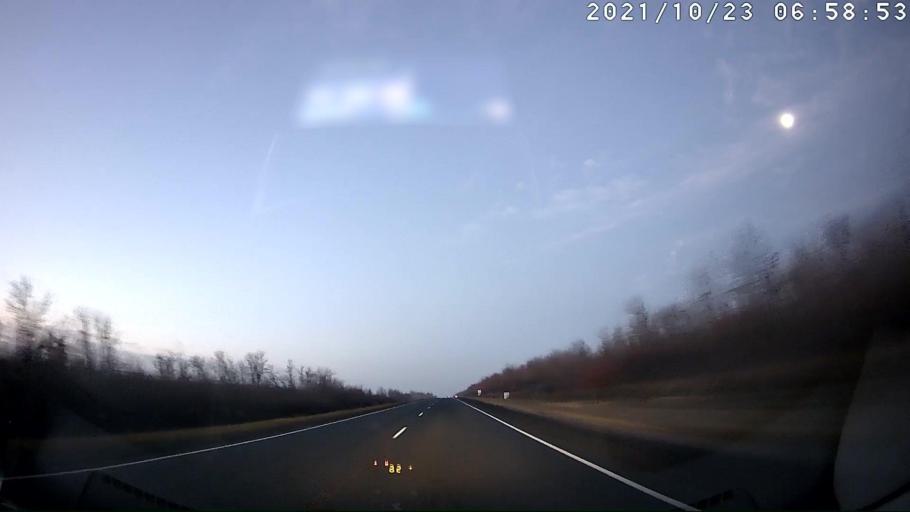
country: RU
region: Saratov
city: Dukhovnitskoye
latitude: 52.6888
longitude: 48.2413
